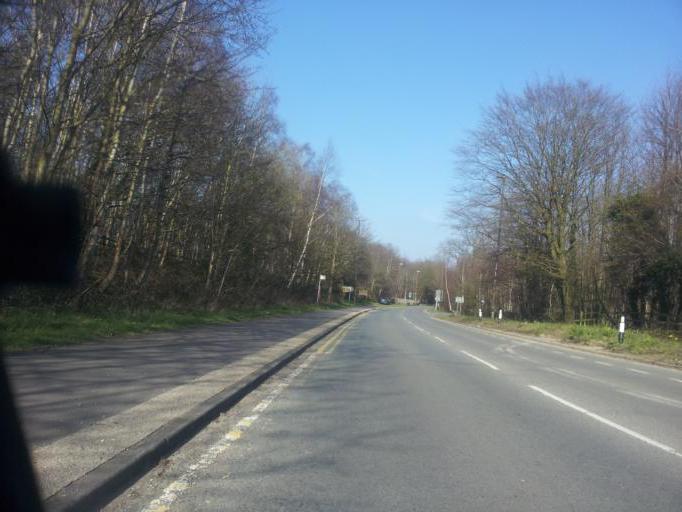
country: GB
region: England
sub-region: Medway
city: Cuxton
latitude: 51.4025
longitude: 0.4197
